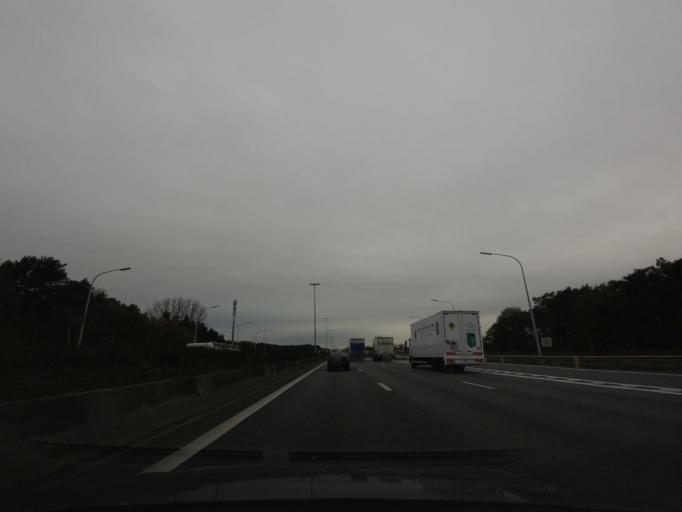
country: BE
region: Flanders
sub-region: Provincie Oost-Vlaanderen
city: Waasmunster
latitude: 51.1318
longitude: 4.1141
